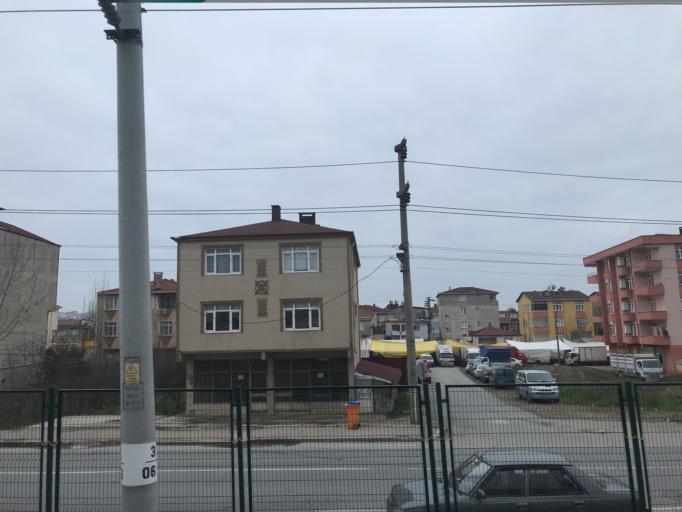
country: TR
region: Kocaeli
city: Darica
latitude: 40.7887
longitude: 29.3957
